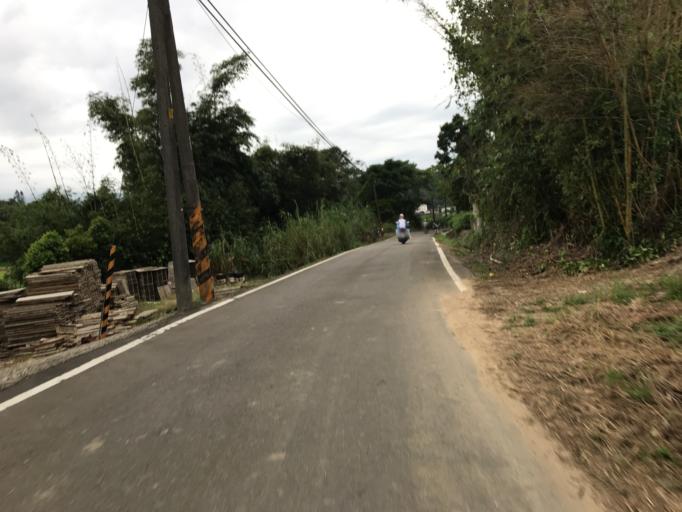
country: TW
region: Taiwan
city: Daxi
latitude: 24.7799
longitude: 121.1746
